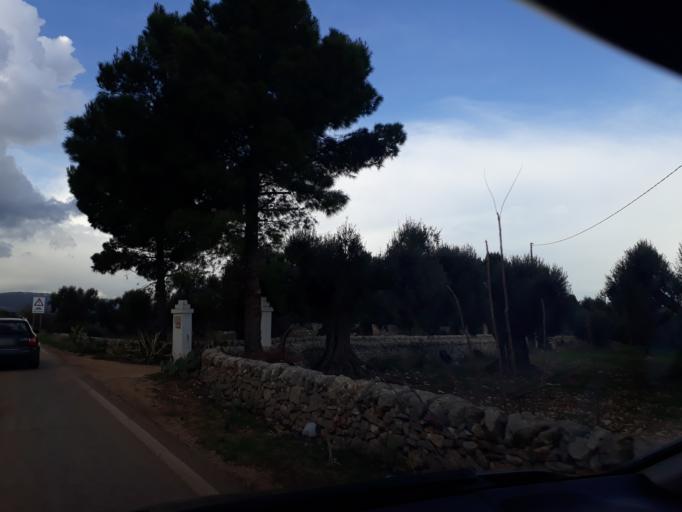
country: IT
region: Apulia
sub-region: Provincia di Brindisi
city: Pezze di Greco
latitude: 40.7993
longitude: 17.4073
